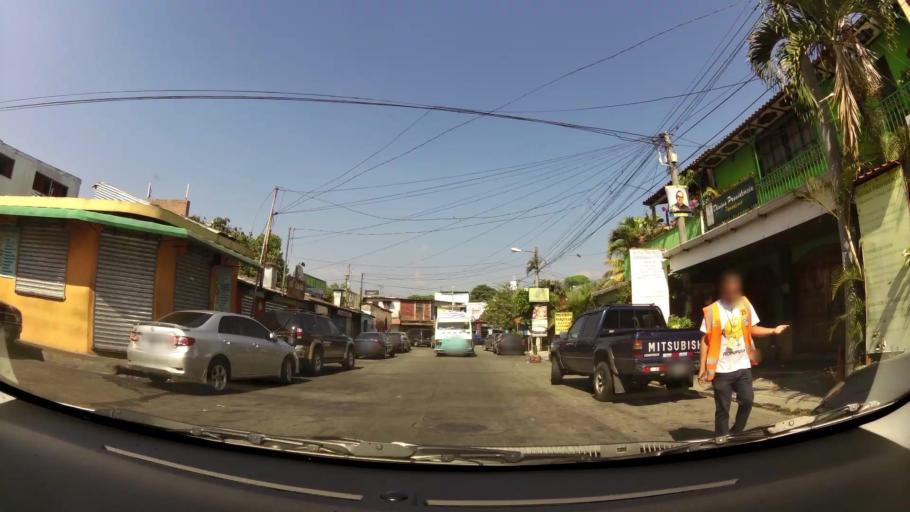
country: SV
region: La Libertad
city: Antiguo Cuscatlan
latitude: 13.6737
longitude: -89.2412
